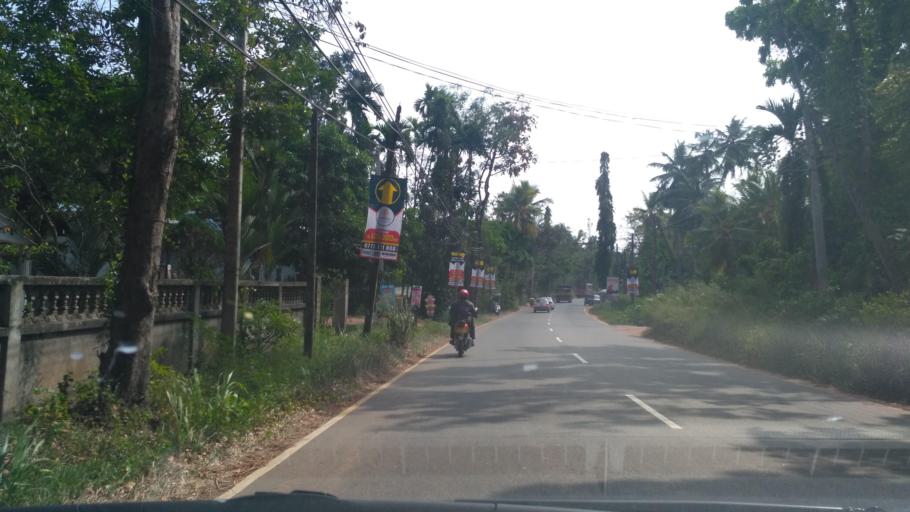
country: LK
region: North Western
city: Kuliyapitiya
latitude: 7.3370
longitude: 80.0305
